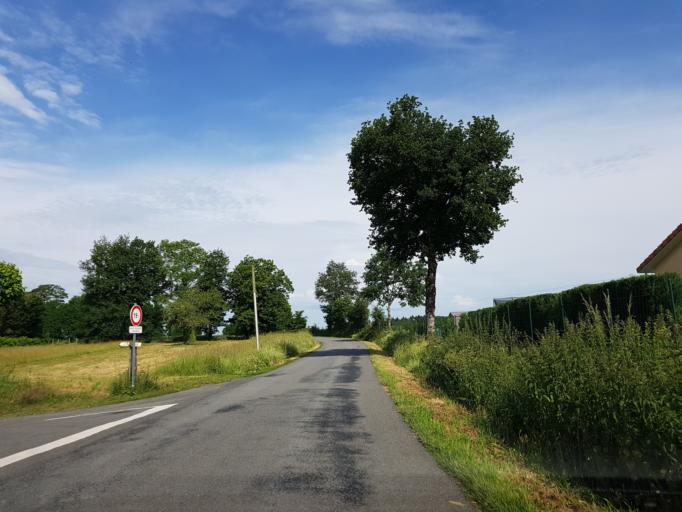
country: FR
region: Poitou-Charentes
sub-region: Departement de la Charente
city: Chabanais
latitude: 45.8885
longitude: 0.6992
